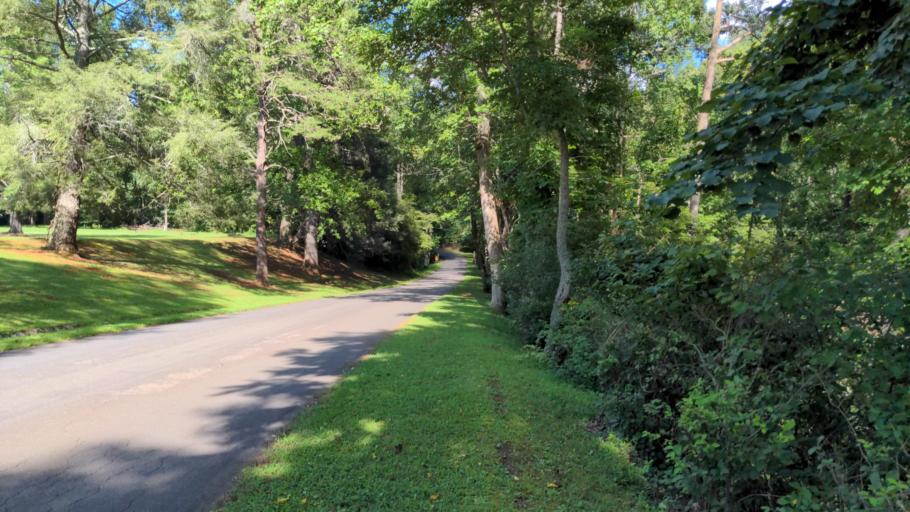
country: US
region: Virginia
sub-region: Henry County
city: Bassett
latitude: 36.7932
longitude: -80.1155
